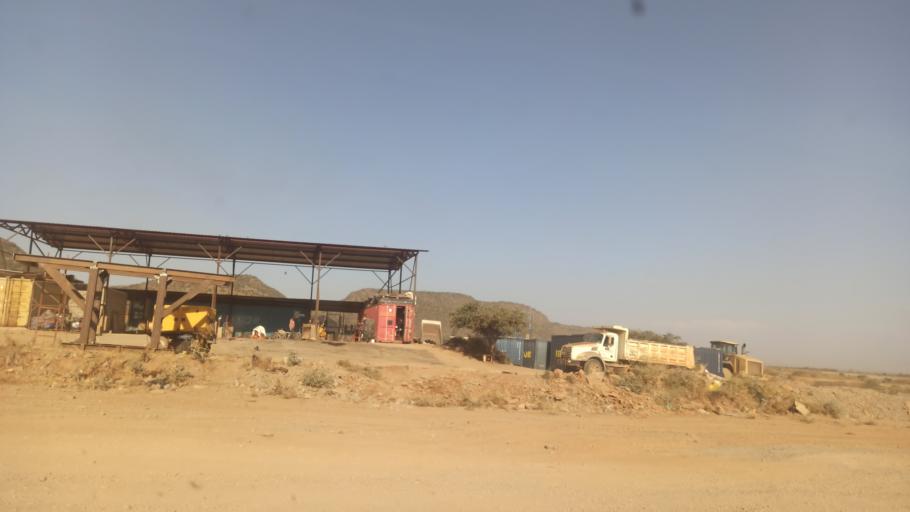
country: ET
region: Oromiya
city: Ziway
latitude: 7.9349
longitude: 38.6143
